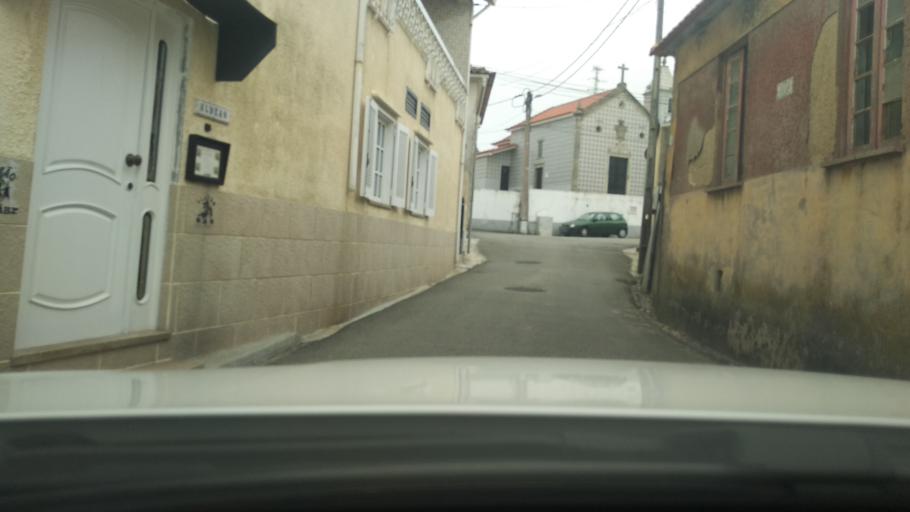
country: PT
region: Aveiro
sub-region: Espinho
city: Silvalde
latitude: 40.9972
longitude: -8.6314
